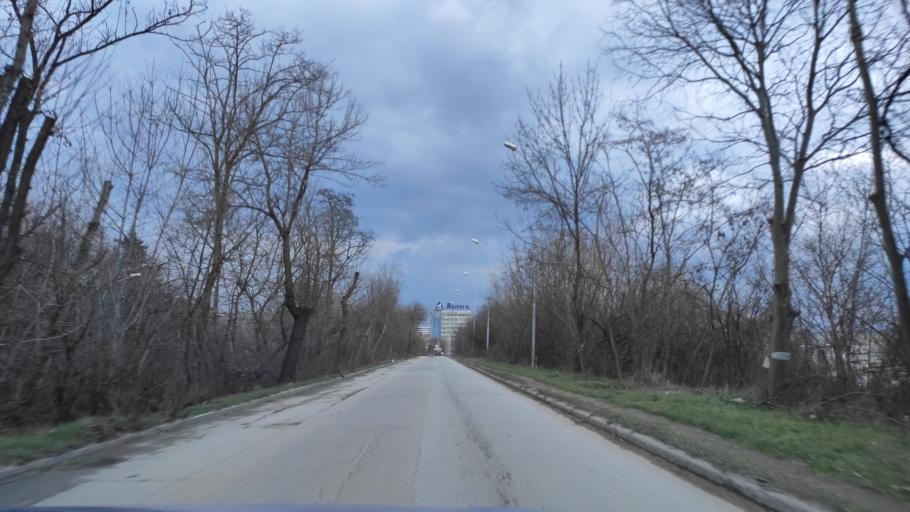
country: BG
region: Varna
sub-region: Obshtina Varna
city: Varna
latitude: 43.2237
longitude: 27.8656
